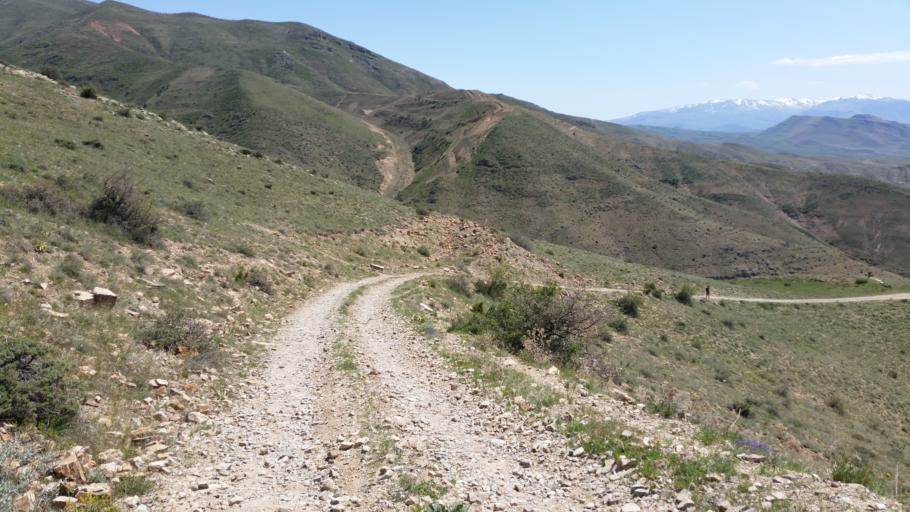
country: AM
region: Vayots' Dzori Marz
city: Vernashen
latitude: 39.8033
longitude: 45.3592
